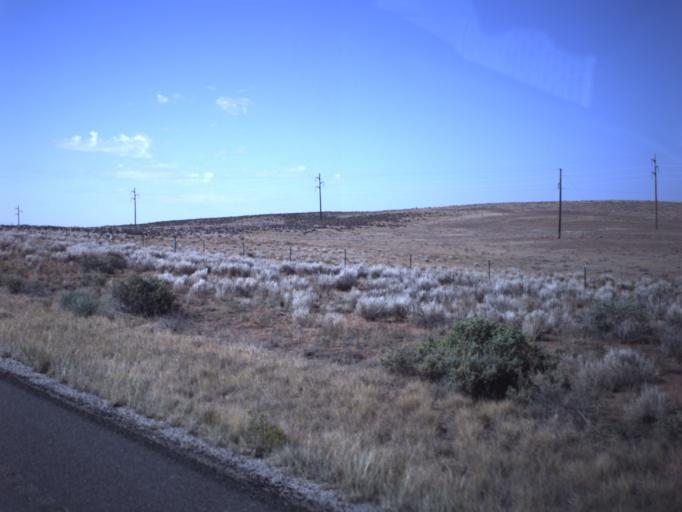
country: US
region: Utah
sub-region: San Juan County
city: Blanding
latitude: 37.3994
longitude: -109.4946
